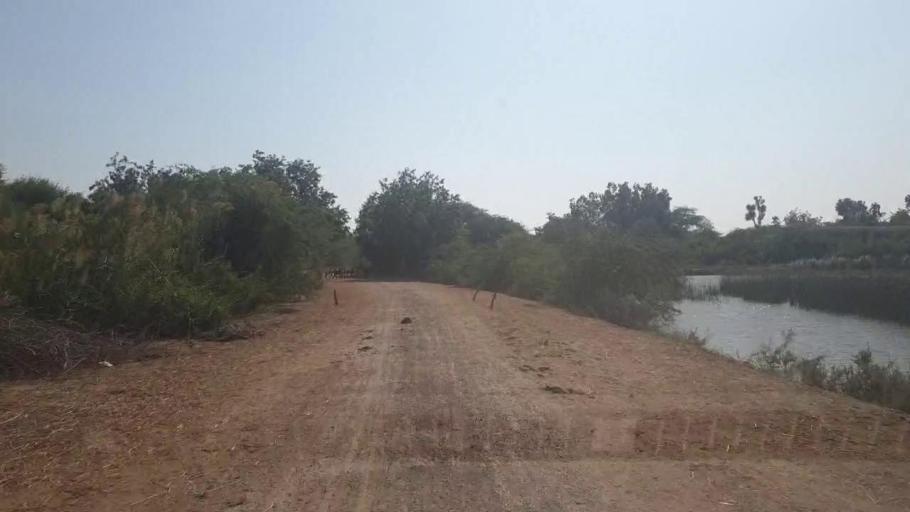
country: PK
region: Sindh
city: Badin
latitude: 24.5468
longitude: 68.8446
